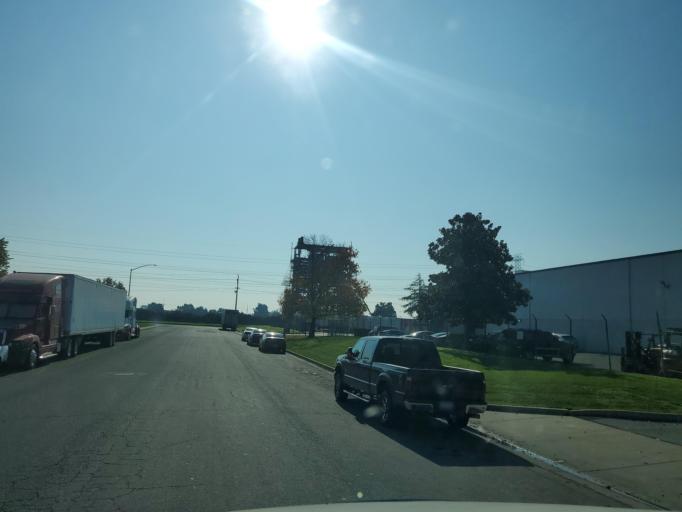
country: US
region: California
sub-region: San Joaquin County
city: Kennedy
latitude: 37.9150
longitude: -121.2618
